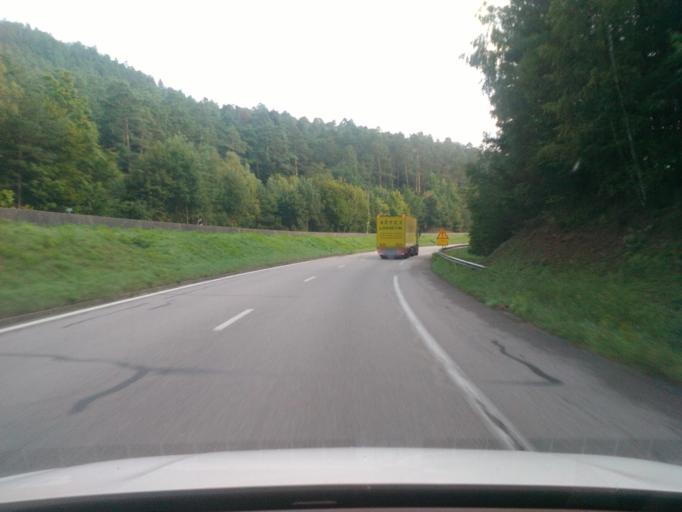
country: FR
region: Lorraine
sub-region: Departement des Vosges
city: Saint-Die-des-Vosges
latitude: 48.2668
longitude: 6.9417
